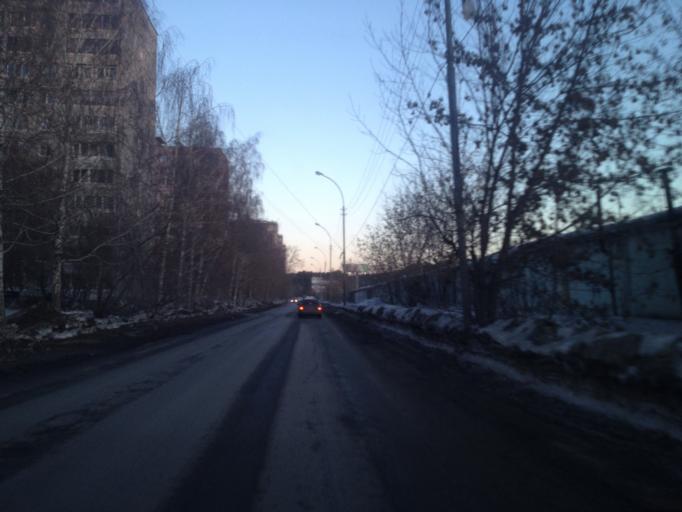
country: RU
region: Sverdlovsk
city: Sovkhoznyy
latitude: 56.7934
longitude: 60.5704
